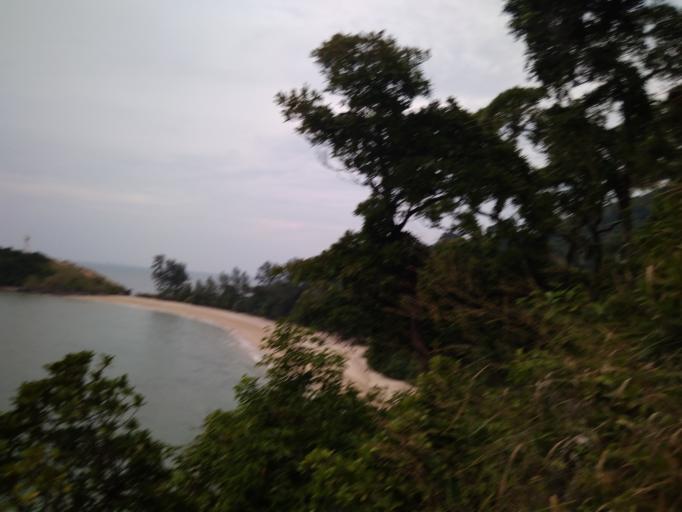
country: TH
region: Krabi
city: Ko Lanta
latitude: 7.4697
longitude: 99.1018
